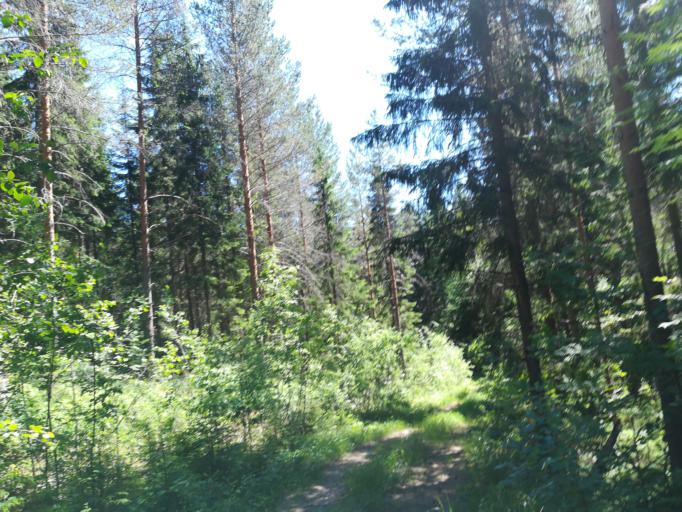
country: FI
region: Southern Savonia
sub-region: Mikkeli
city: Puumala
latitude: 61.6166
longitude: 28.1621
